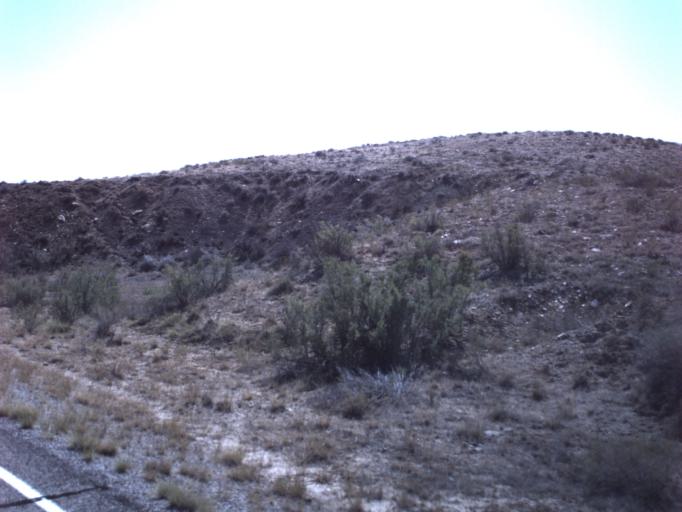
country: US
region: Utah
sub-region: Grand County
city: Moab
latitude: 38.8586
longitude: -109.2923
